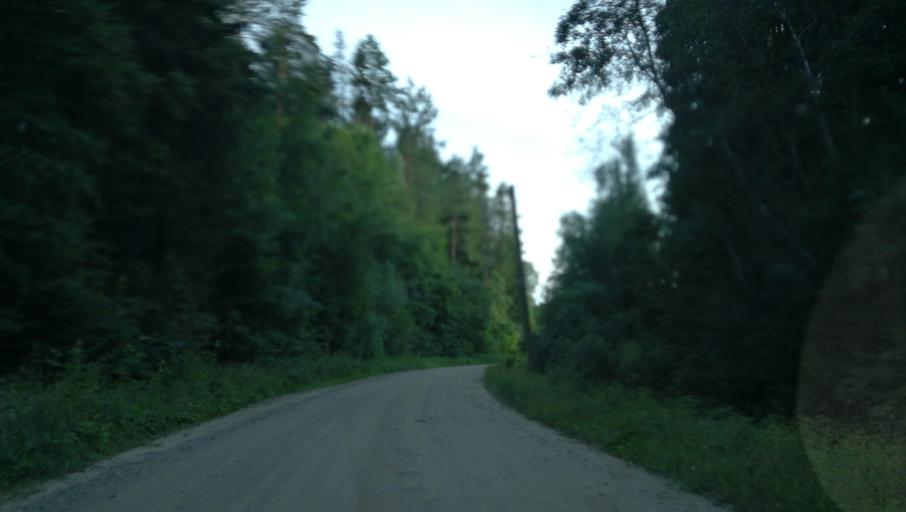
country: LV
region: Cesu Rajons
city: Cesis
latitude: 57.3465
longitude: 25.1873
